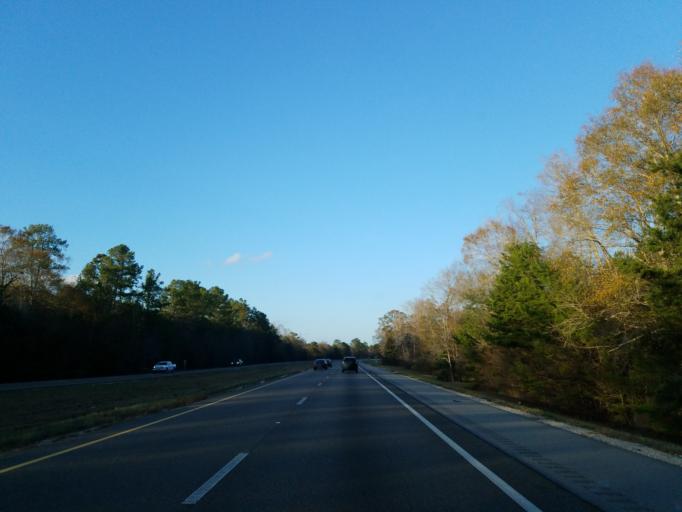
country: US
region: Mississippi
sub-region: Clarke County
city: Stonewall
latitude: 32.0895
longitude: -88.8931
